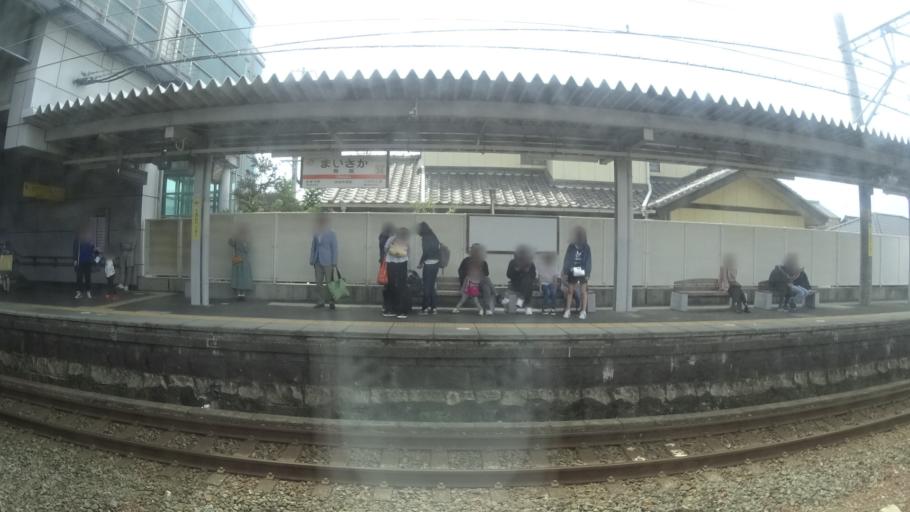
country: JP
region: Shizuoka
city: Kosai-shi
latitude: 34.6856
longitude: 137.6269
